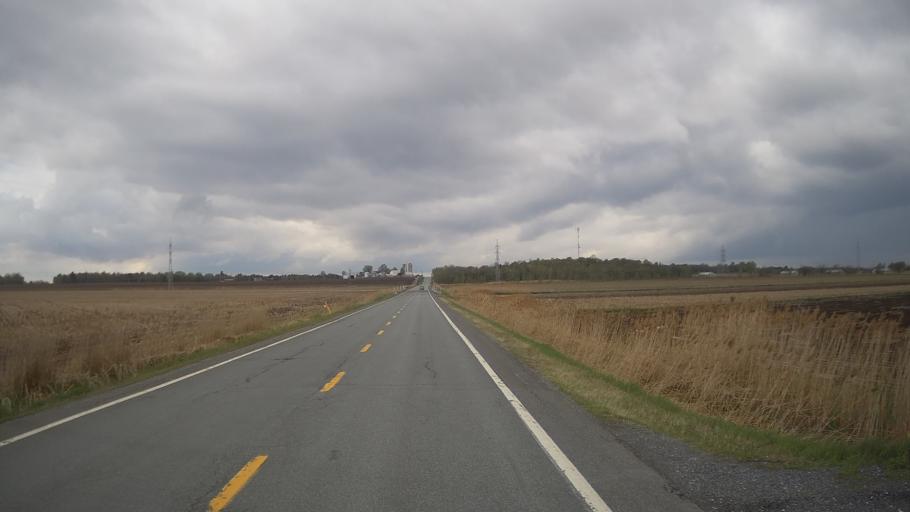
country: CA
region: Quebec
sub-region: Monteregie
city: Farnham
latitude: 45.2613
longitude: -72.9275
